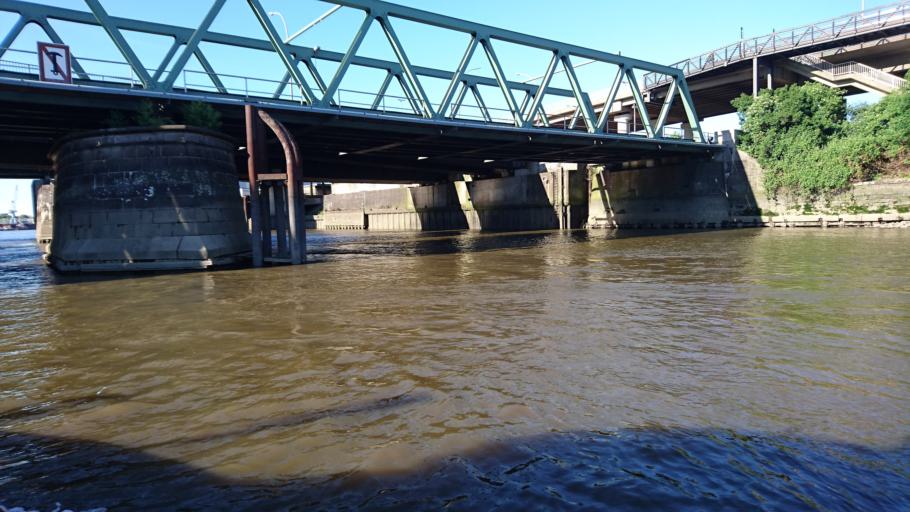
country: DE
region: Hamburg
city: Kleiner Grasbrook
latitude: 53.5271
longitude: 9.9767
